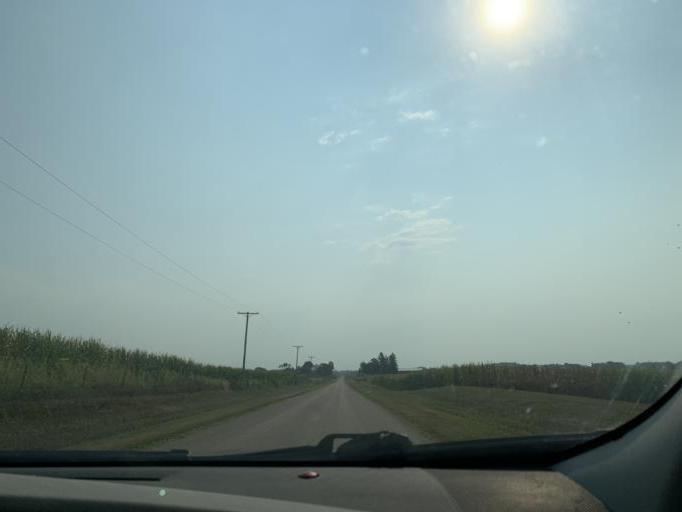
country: US
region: Illinois
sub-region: Whiteside County
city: Morrison
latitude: 41.8697
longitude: -89.9129
